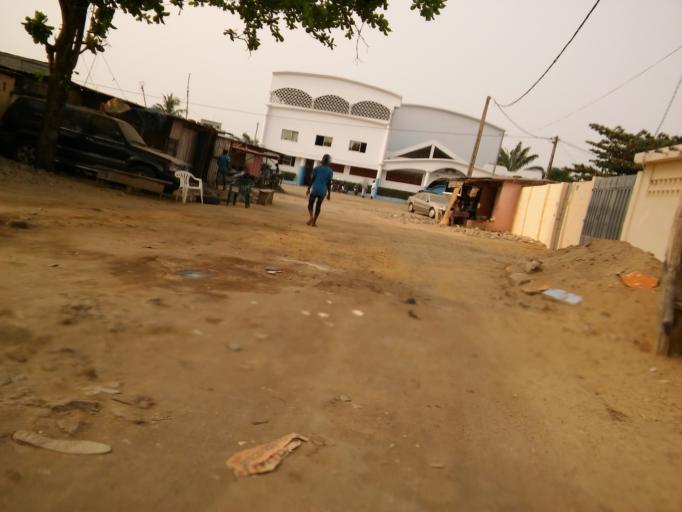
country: BJ
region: Littoral
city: Cotonou
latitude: 6.3592
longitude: 2.4033
